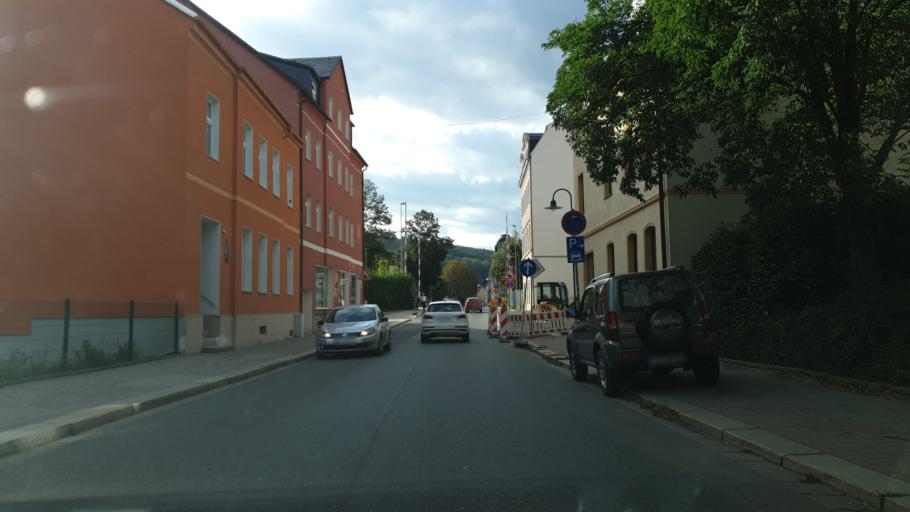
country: DE
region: Saxony
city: Aue
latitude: 50.5857
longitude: 12.7089
